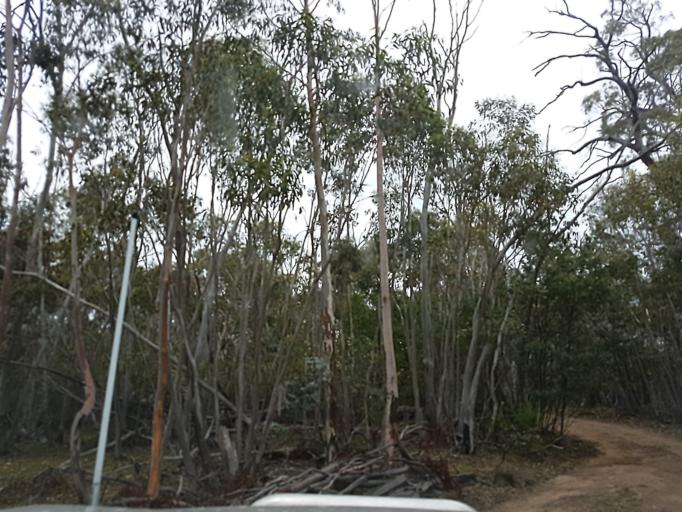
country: AU
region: New South Wales
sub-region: Snowy River
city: Jindabyne
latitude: -36.8594
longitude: 148.2646
